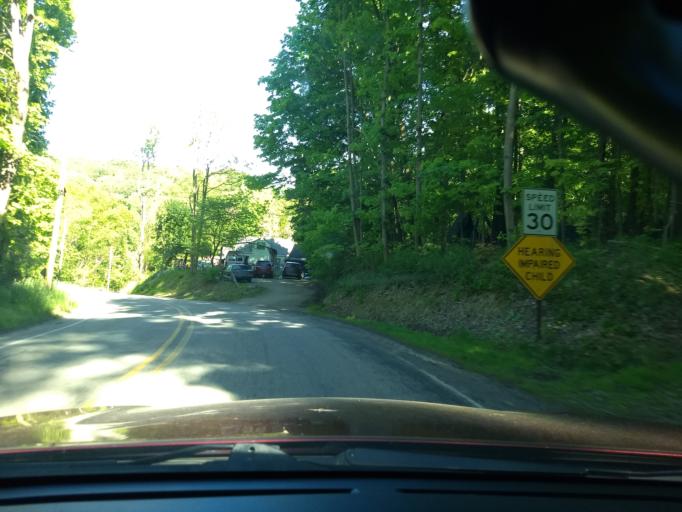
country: US
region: Pennsylvania
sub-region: Allegheny County
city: Versailles
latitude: 40.3000
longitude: -79.8454
